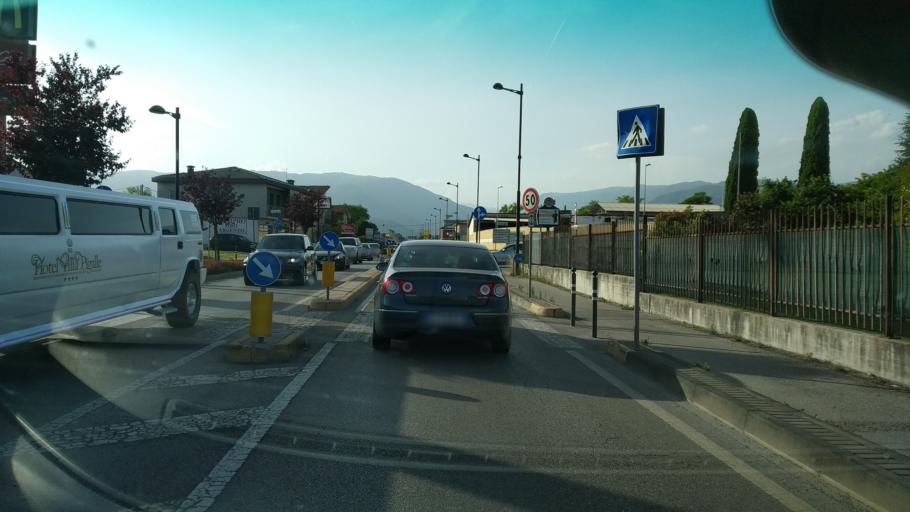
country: IT
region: Veneto
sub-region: Provincia di Vicenza
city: San Zeno-San Giuseppe
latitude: 45.7462
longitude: 11.7522
